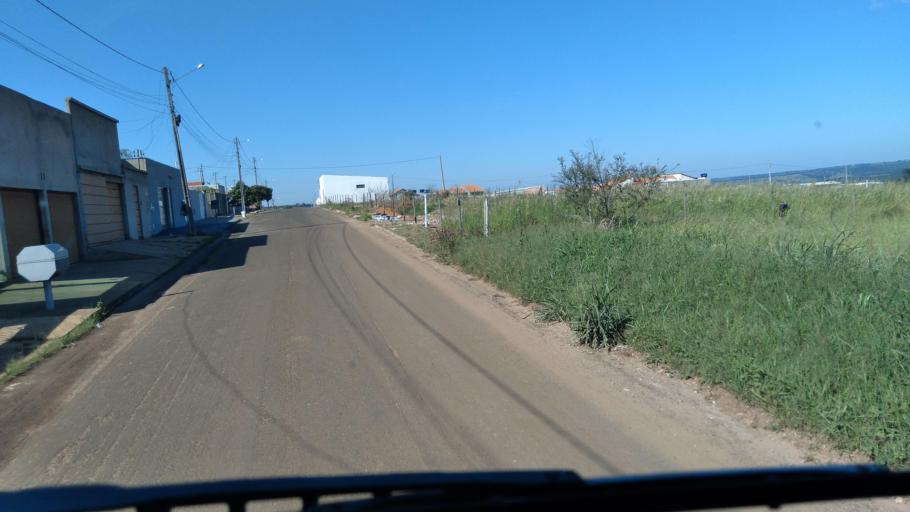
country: BR
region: Goias
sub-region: Mineiros
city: Mineiros
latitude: -17.5743
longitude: -52.5761
